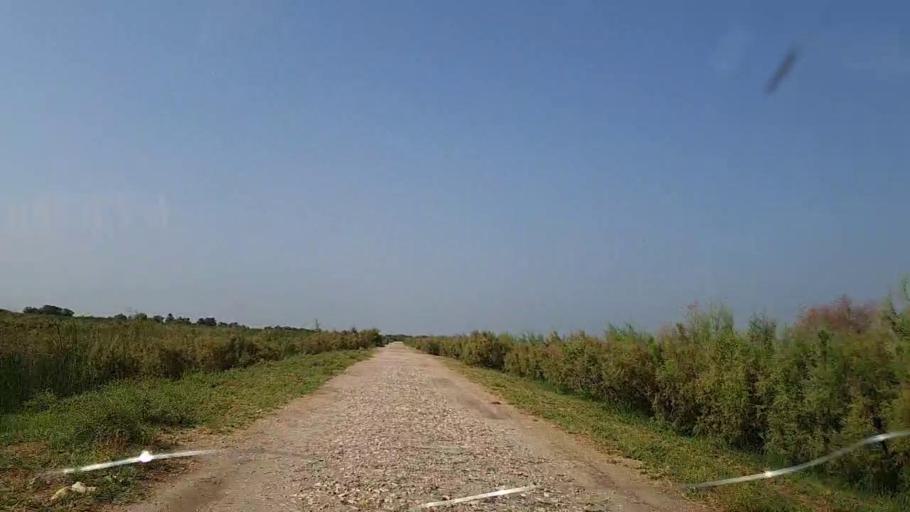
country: PK
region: Sindh
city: Khanpur
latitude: 27.7007
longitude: 69.3855
